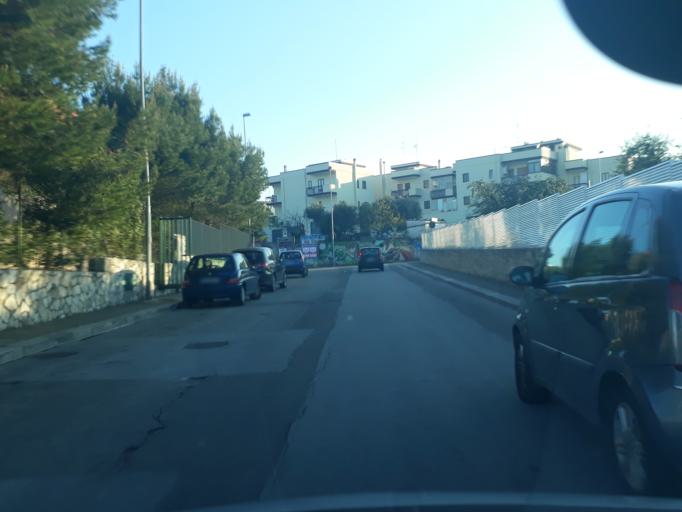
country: IT
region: Apulia
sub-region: Provincia di Bari
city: Locorotondo
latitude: 40.7601
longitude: 17.3257
